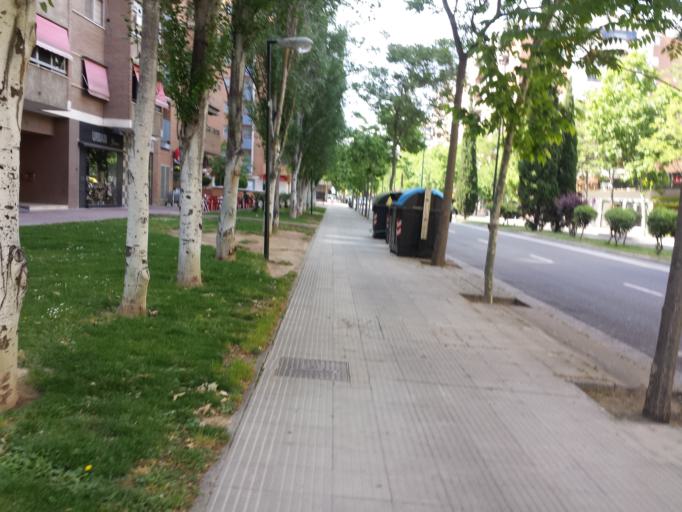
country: ES
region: Aragon
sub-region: Provincia de Zaragoza
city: Zaragoza
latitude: 41.6713
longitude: -0.8769
